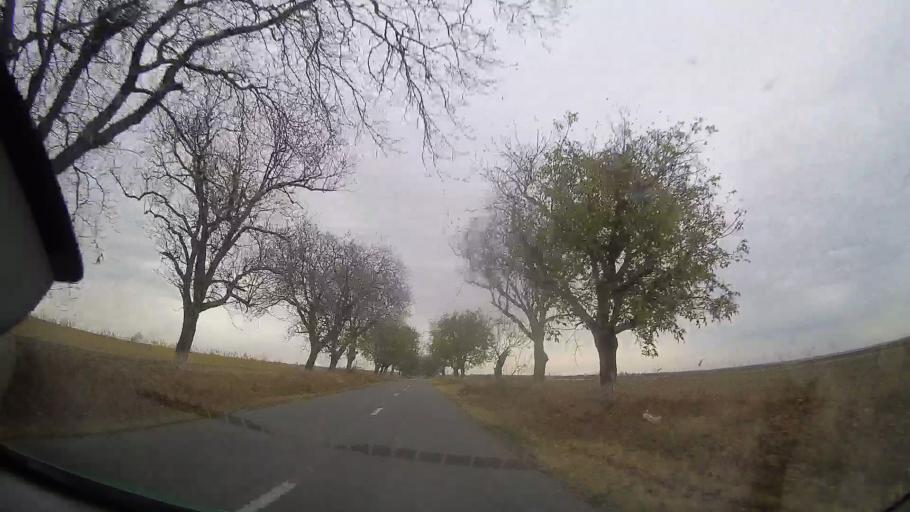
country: RO
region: Prahova
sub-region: Comuna Fantanele
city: Fantanele
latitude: 45.0152
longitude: 26.4049
